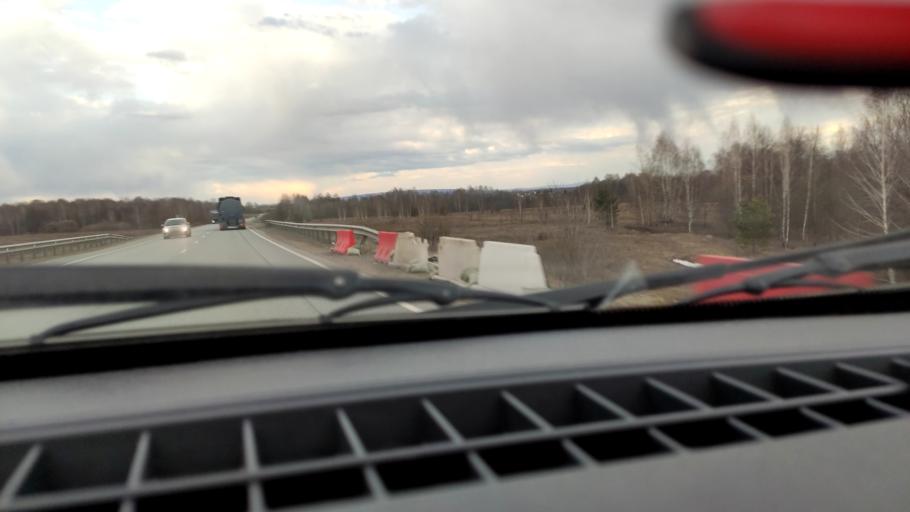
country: RU
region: Bashkortostan
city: Kudeyevskiy
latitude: 54.8153
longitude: 56.6953
